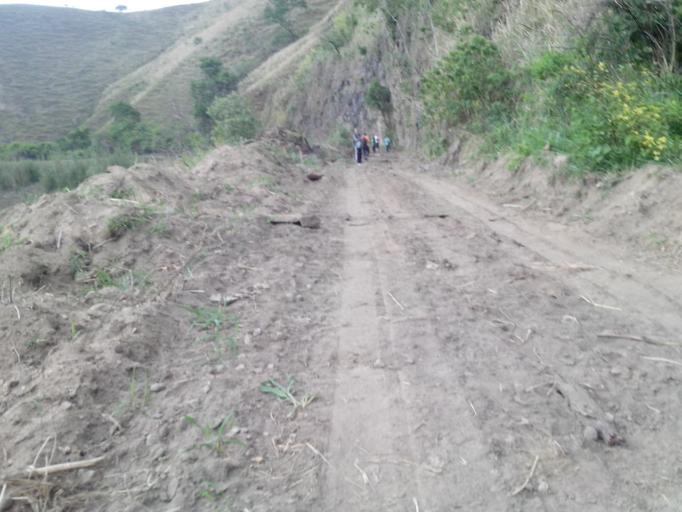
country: BR
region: Rio de Janeiro
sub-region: Miguel Pereira
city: Miguel Pereira
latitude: -22.5002
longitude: -43.4996
